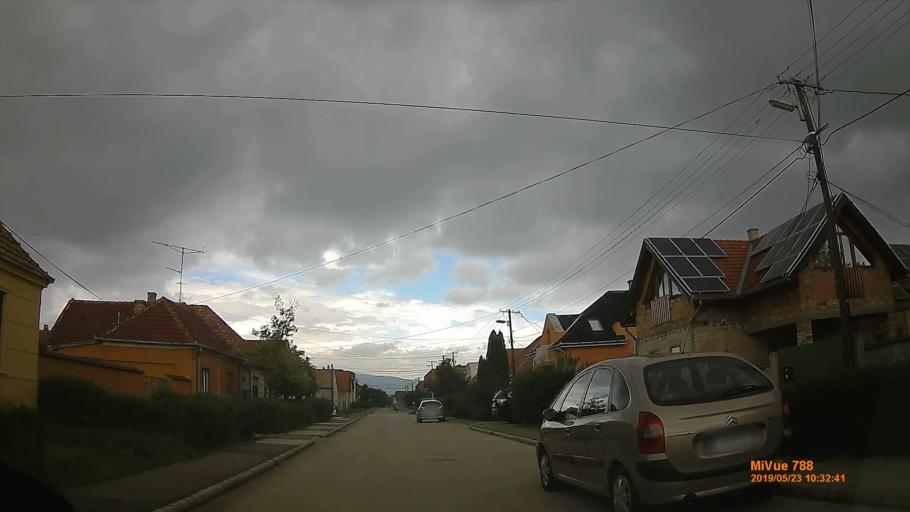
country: HU
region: Veszprem
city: Veszprem
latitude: 47.1034
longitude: 17.9009
